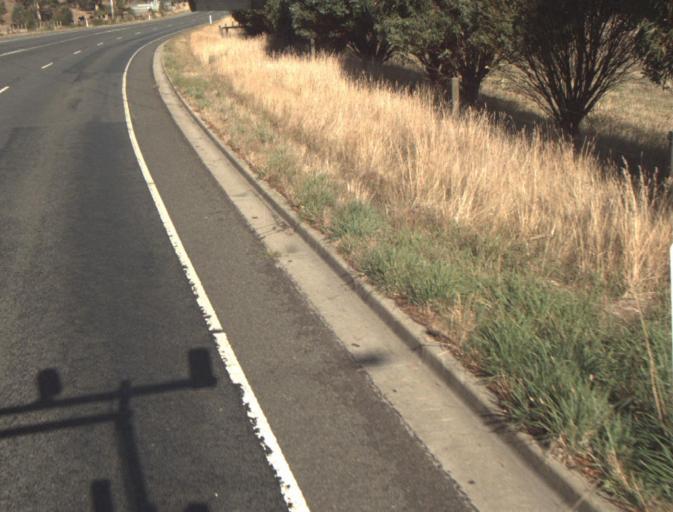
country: AU
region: Tasmania
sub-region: Launceston
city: Mayfield
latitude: -41.3433
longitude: 147.0922
